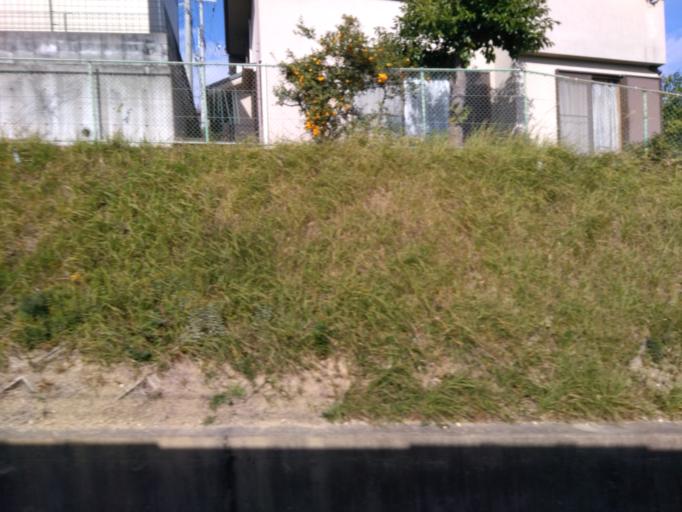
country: JP
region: Hyogo
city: Takarazuka
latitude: 34.8206
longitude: 135.3737
